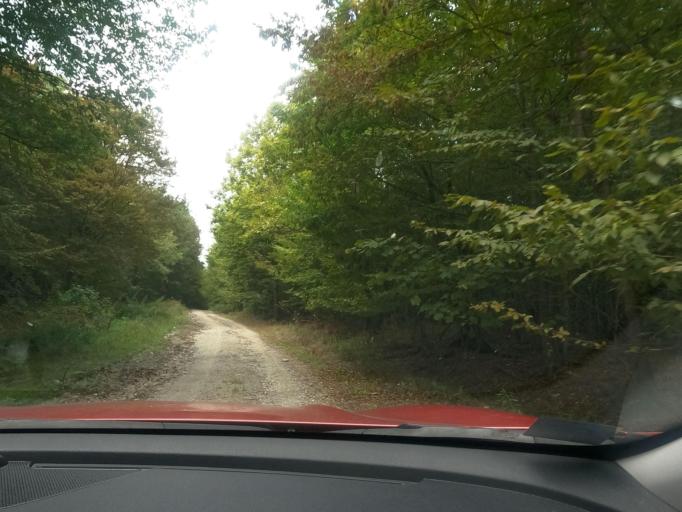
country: BA
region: Federation of Bosnia and Herzegovina
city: Velika Kladusa
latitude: 45.2594
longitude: 15.7881
